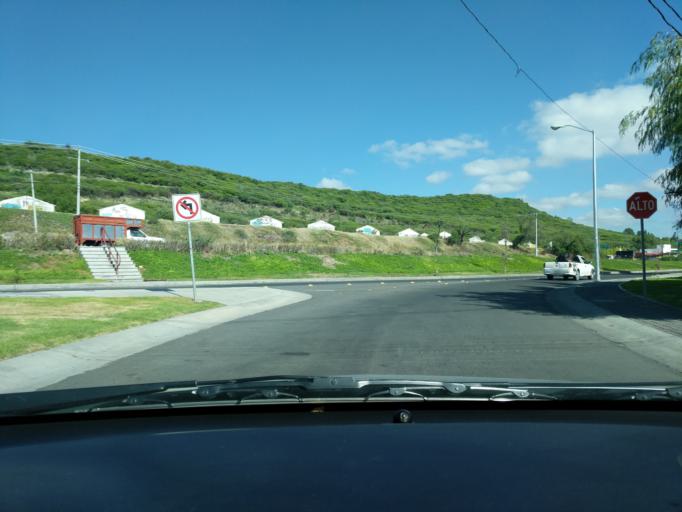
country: MX
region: Queretaro
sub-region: Queretaro
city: Patria Nueva
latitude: 20.6116
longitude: -100.4925
